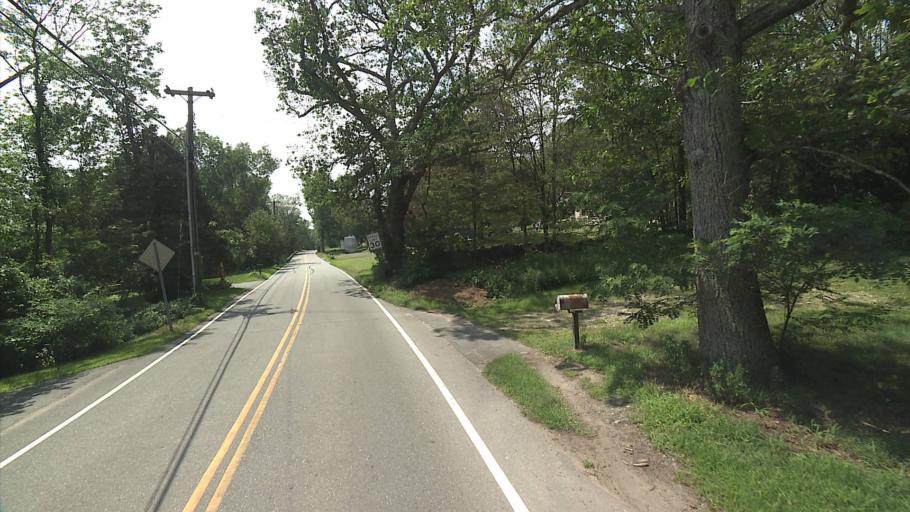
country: US
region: Connecticut
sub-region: Windham County
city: Moosup
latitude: 41.7395
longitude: -71.8558
